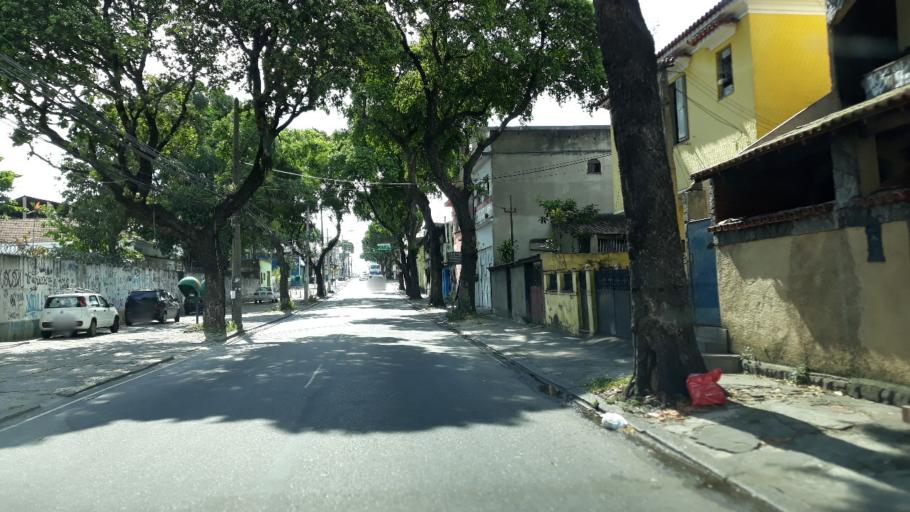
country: BR
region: Rio de Janeiro
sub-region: Sao Joao De Meriti
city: Sao Joao de Meriti
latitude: -22.8651
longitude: -43.3585
